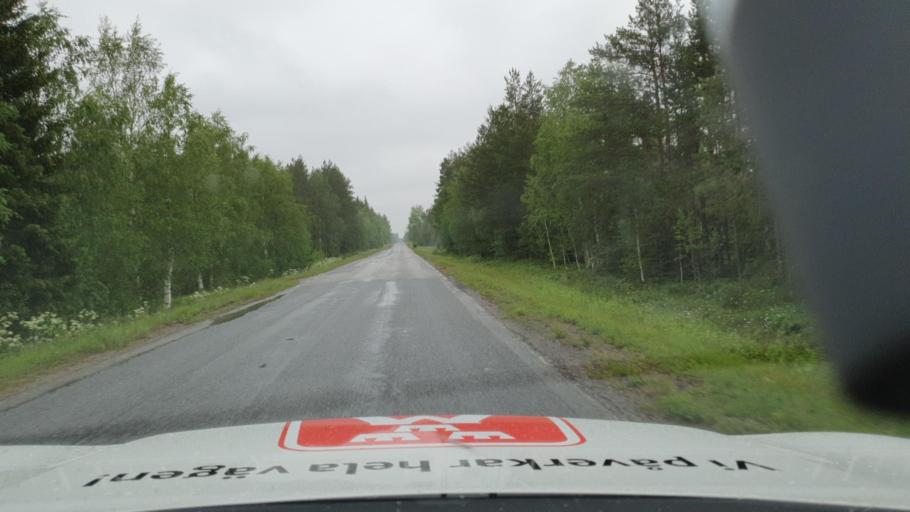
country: SE
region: Vaesterbotten
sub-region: Nordmalings Kommun
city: Nordmaling
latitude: 63.8156
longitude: 19.4973
